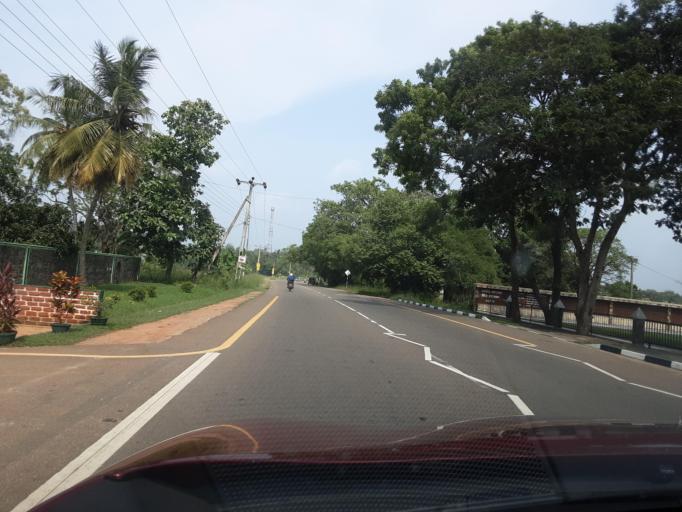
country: LK
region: North Central
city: Anuradhapura
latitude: 8.3614
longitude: 80.5111
